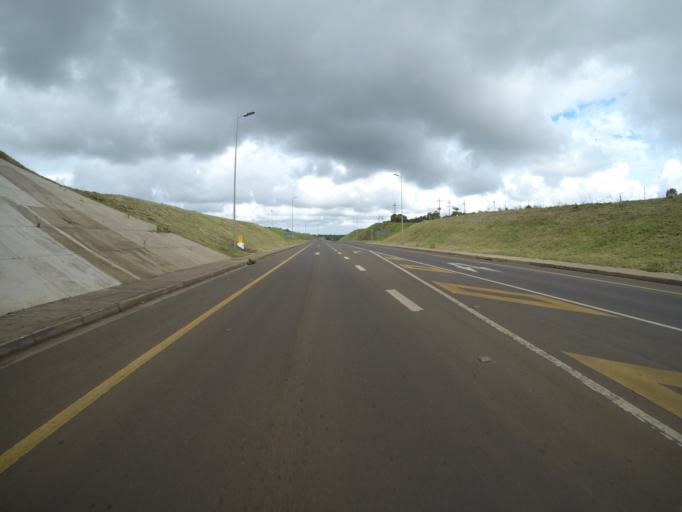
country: ZA
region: KwaZulu-Natal
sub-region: uMkhanyakude District Municipality
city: Mtubatuba
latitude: -28.4169
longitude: 32.1637
